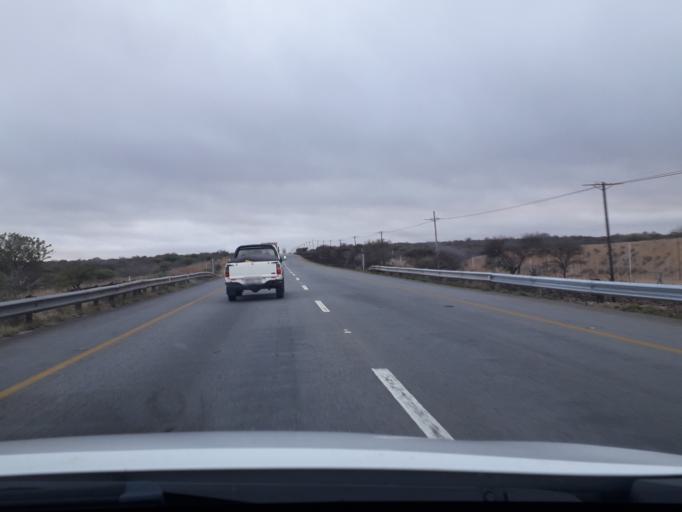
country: ZA
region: Limpopo
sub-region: Capricorn District Municipality
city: Mankoeng
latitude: -23.5922
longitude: 29.6610
